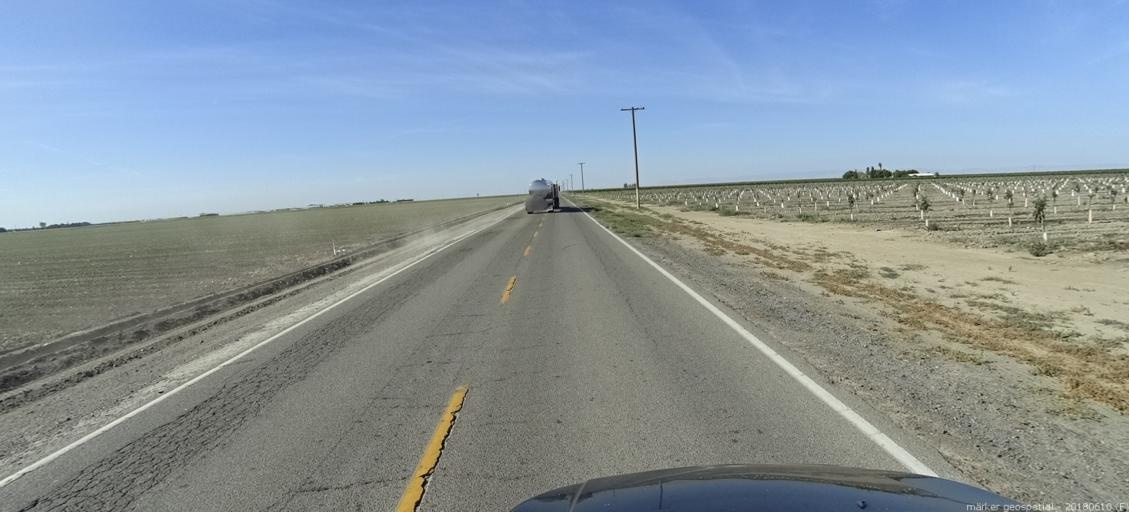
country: US
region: California
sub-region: Madera County
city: Fairmead
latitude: 36.9439
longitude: -120.2555
